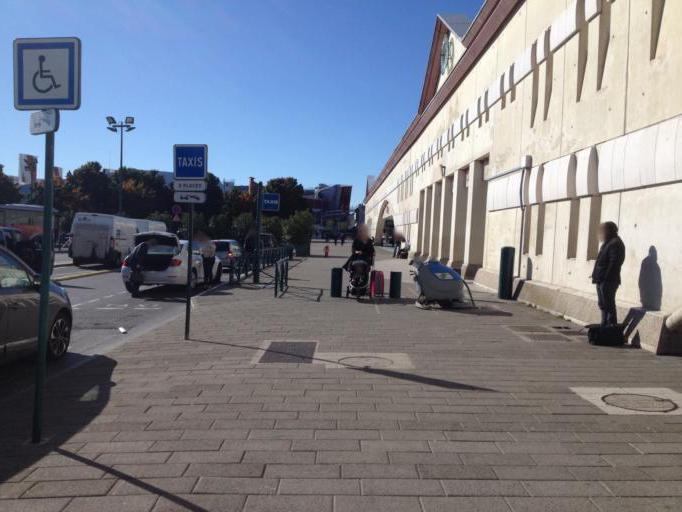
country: FR
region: Ile-de-France
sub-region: Departement de Seine-et-Marne
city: Chessy
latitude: 48.8709
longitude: 2.7833
